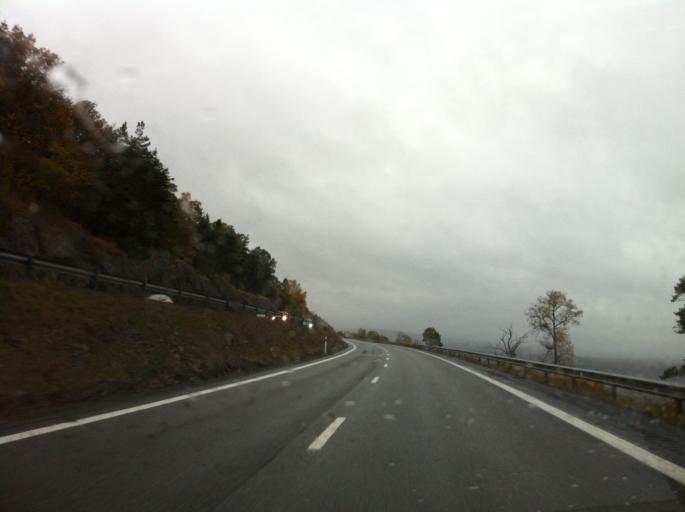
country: SE
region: Joenkoeping
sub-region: Jonkopings Kommun
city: Kaxholmen
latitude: 57.8634
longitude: 14.2679
